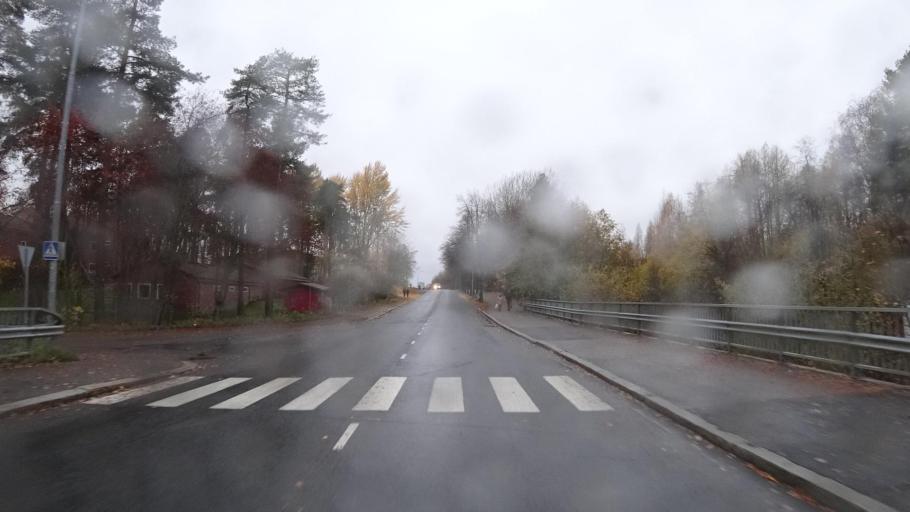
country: FI
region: Northern Savo
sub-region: Kuopio
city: Kuopio
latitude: 62.8978
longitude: 27.7130
